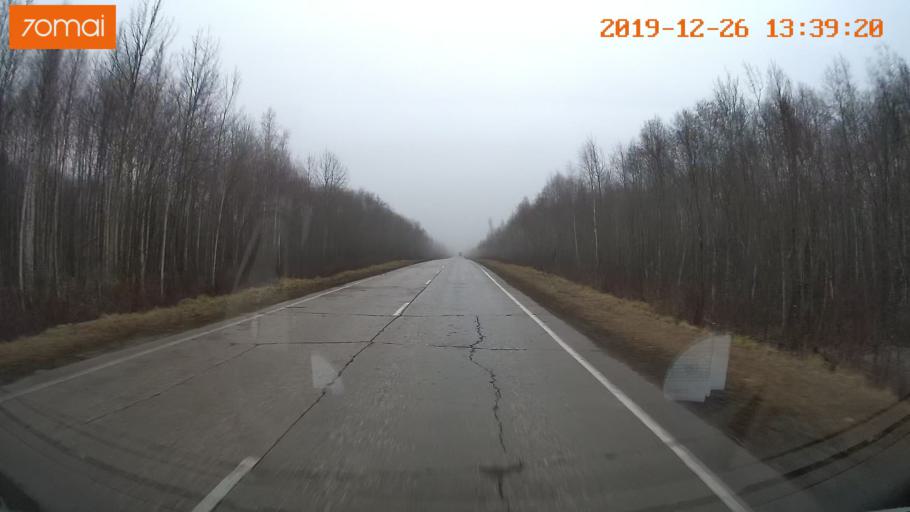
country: RU
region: Vologda
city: Sheksna
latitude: 58.7532
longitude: 38.4091
